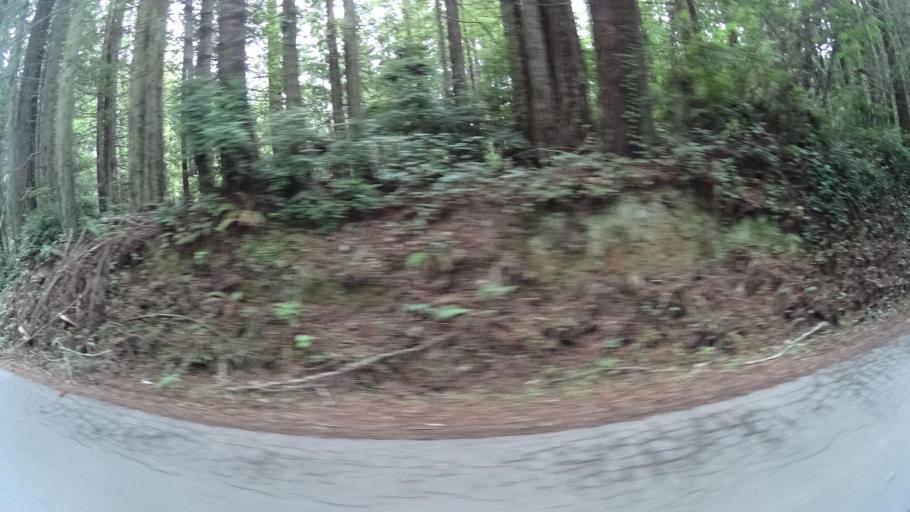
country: US
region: California
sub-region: Humboldt County
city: Bayside
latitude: 40.7951
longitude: -124.0563
